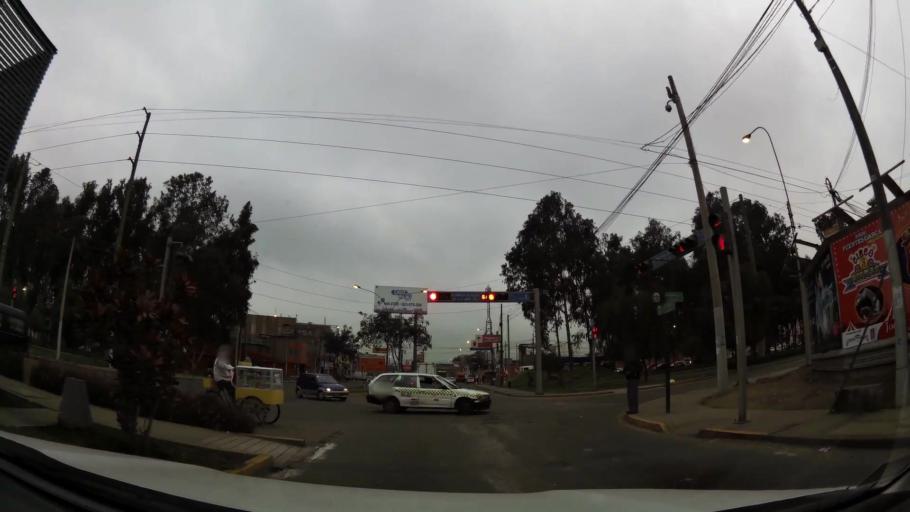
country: PE
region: Lima
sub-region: Lima
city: La Molina
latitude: -12.0649
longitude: -76.9648
